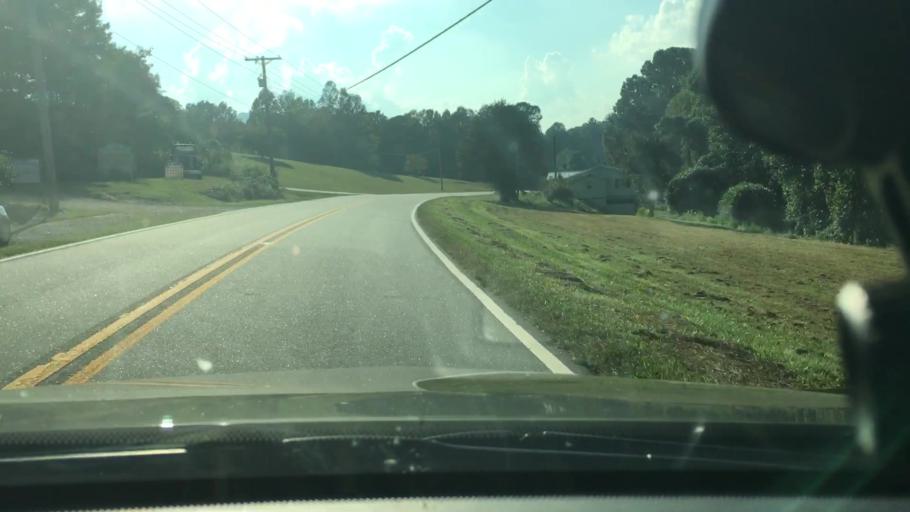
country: US
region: North Carolina
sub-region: Polk County
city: Columbus
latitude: 35.3153
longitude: -82.1359
